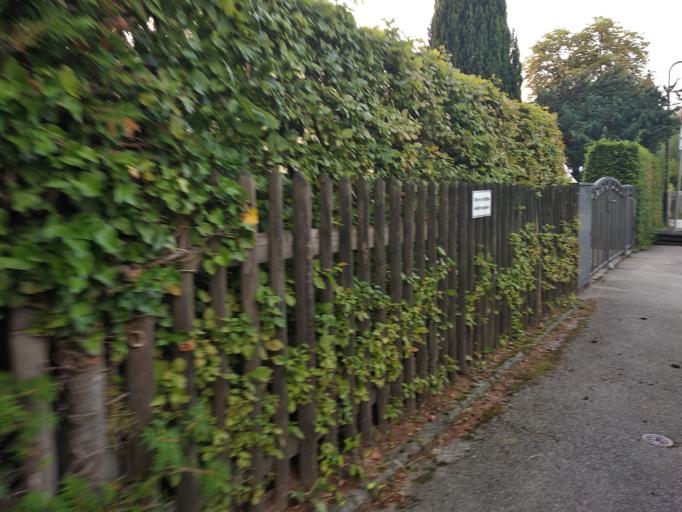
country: DE
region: Bavaria
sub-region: Upper Bavaria
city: Hohenbrunn
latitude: 48.0641
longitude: 11.6938
